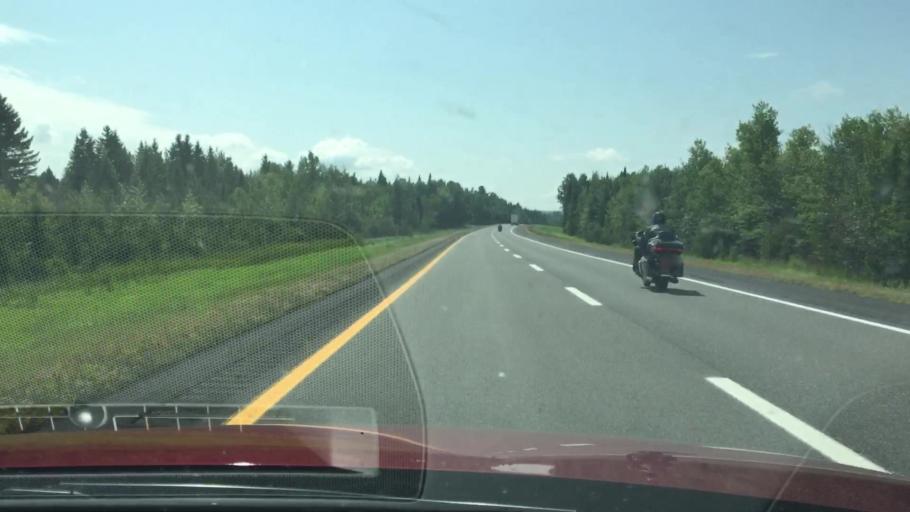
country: US
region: Maine
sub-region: Penobscot County
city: Patten
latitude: 45.9751
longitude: -68.2950
